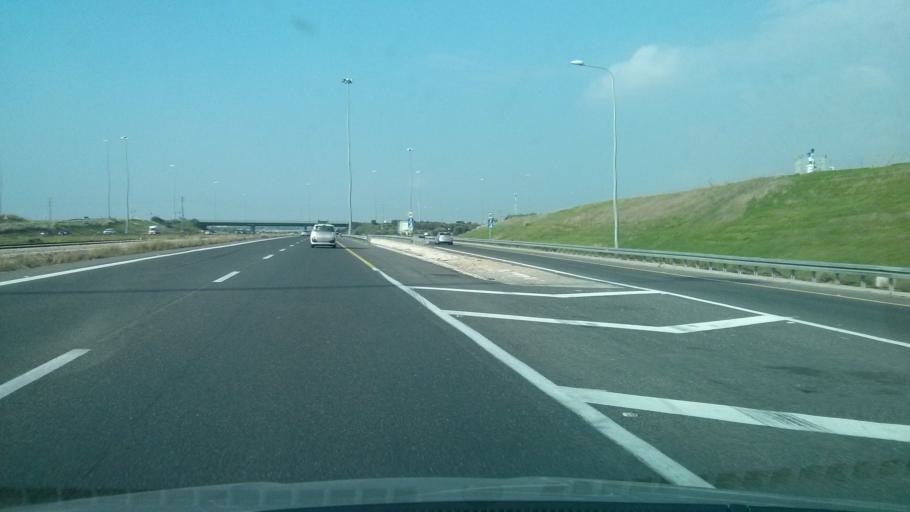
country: IL
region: Central District
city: Gedera
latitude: 31.7889
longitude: 34.8323
